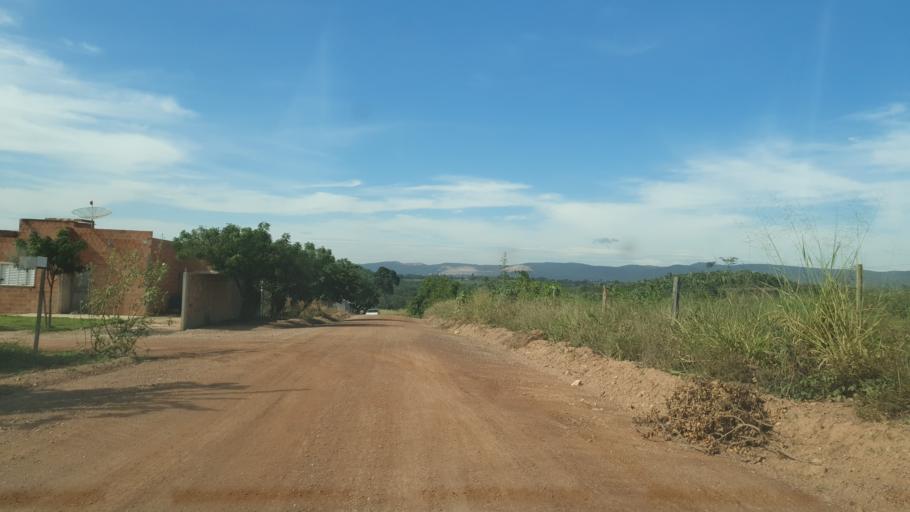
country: BR
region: Mato Grosso
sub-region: Pontes E Lacerda
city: Pontes e Lacerda
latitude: -15.2546
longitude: -59.3145
